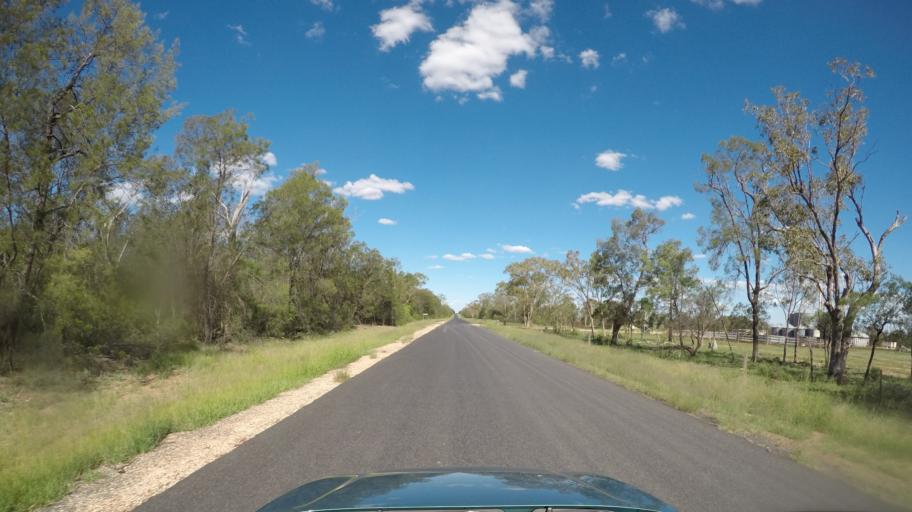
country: AU
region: Queensland
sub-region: Goondiwindi
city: Goondiwindi
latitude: -28.1485
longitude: 150.3149
